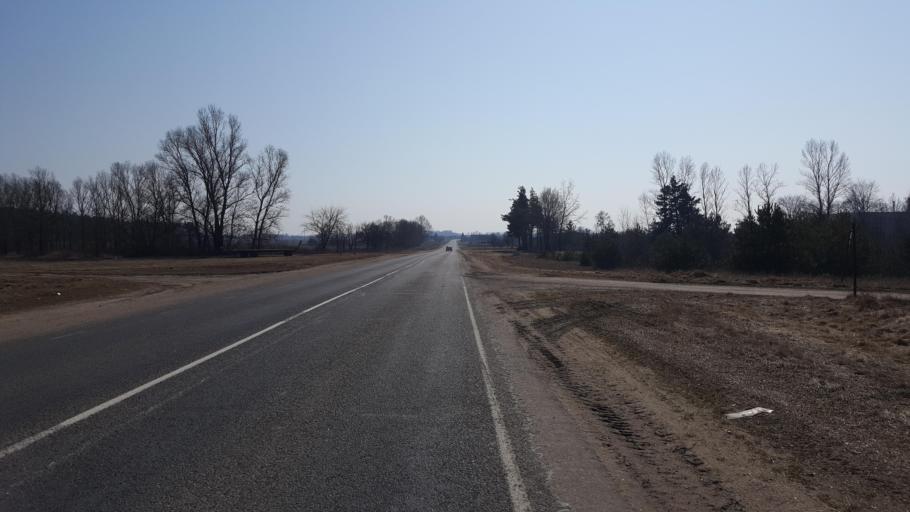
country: BY
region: Brest
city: Kamyanyets
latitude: 52.3364
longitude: 23.9103
